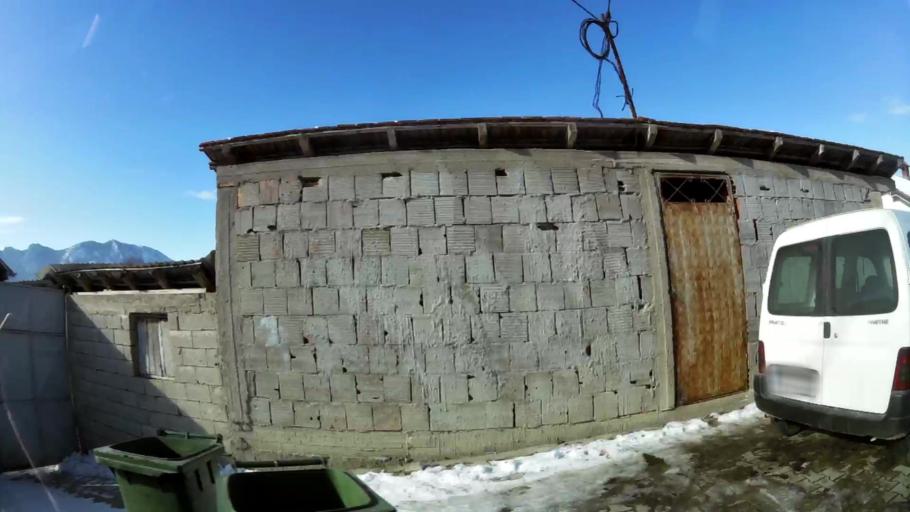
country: MK
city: Grchec
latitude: 41.9904
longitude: 21.3260
